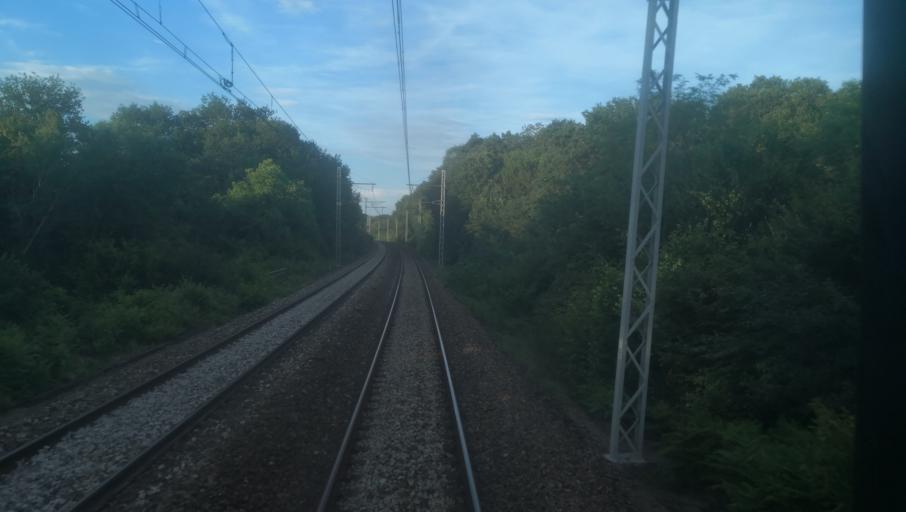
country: FR
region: Centre
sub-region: Departement de l'Indre
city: Saint-Marcel
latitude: 46.6660
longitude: 1.5379
